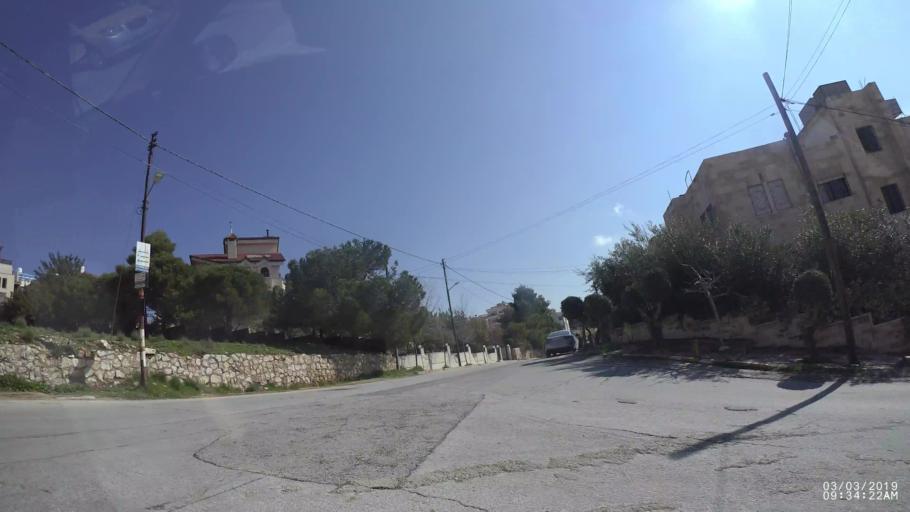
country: JO
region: Amman
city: Al Jubayhah
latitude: 31.9969
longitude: 35.8962
